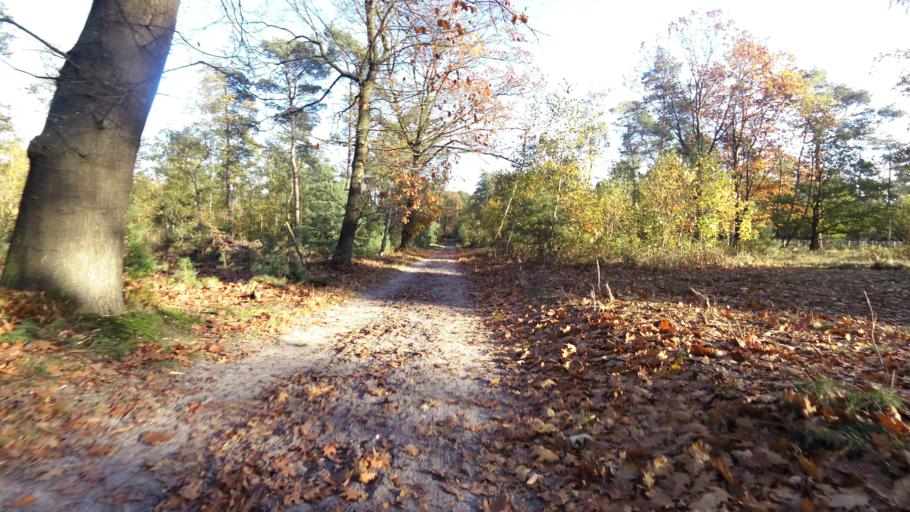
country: NL
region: Gelderland
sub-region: Gemeente Epe
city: Epe
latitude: 52.3982
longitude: 5.9780
